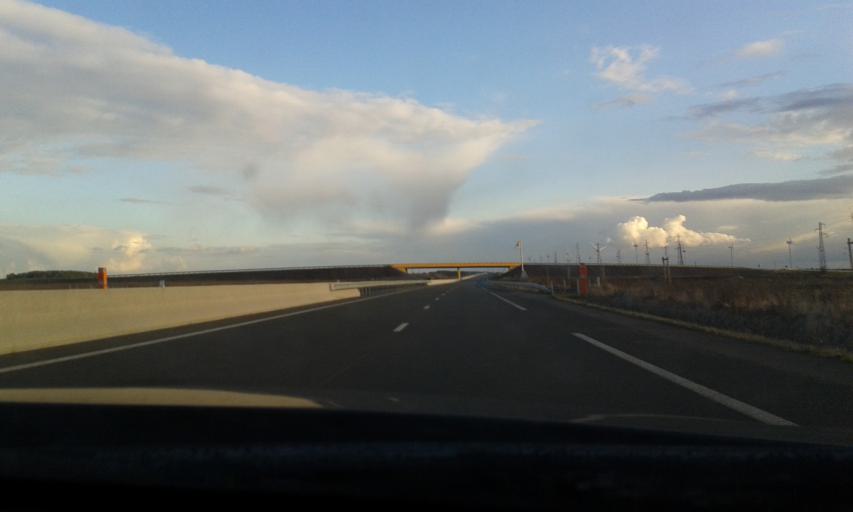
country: FR
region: Centre
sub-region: Departement d'Eure-et-Loir
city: Sours
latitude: 48.3494
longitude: 1.6236
